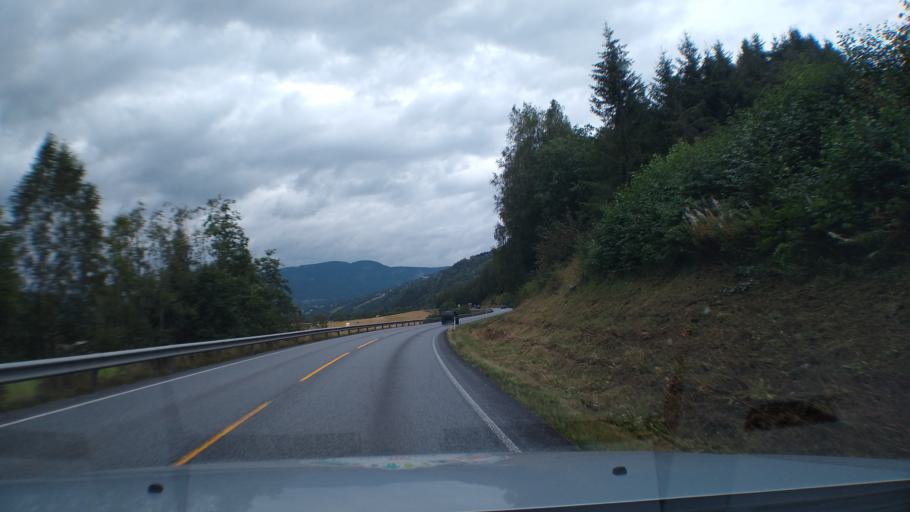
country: NO
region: Oppland
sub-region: Ringebu
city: Ringebu
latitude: 61.5042
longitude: 10.1682
